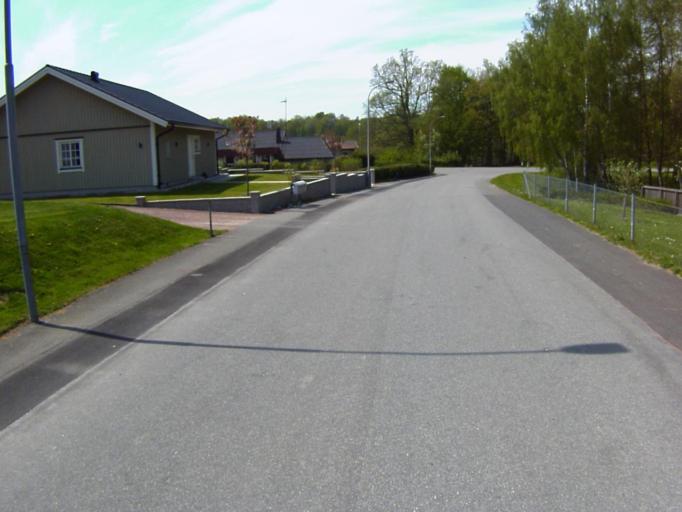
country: SE
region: Skane
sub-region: Kristianstads Kommun
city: Tollarp
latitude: 56.1691
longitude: 14.2908
